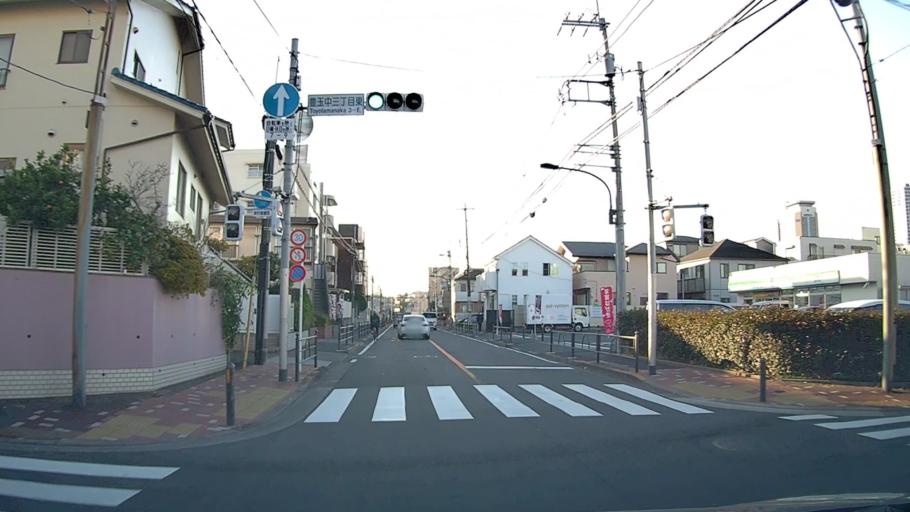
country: JP
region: Tokyo
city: Tokyo
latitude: 35.7323
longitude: 139.6567
